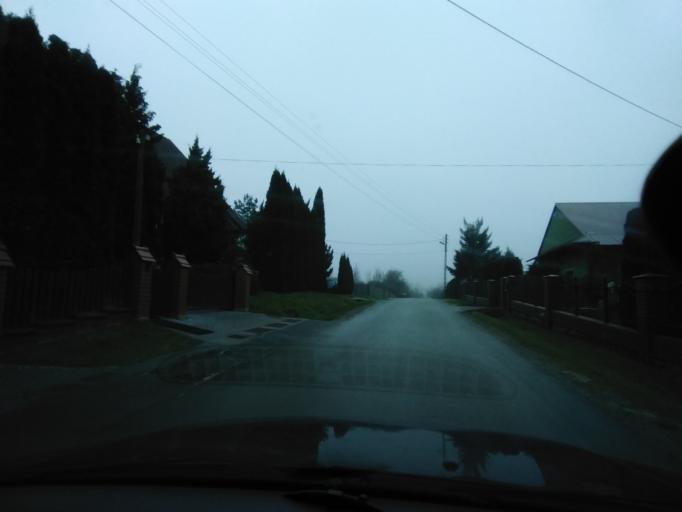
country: PL
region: Subcarpathian Voivodeship
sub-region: Powiat lancucki
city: Markowa
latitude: 50.0251
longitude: 22.3189
